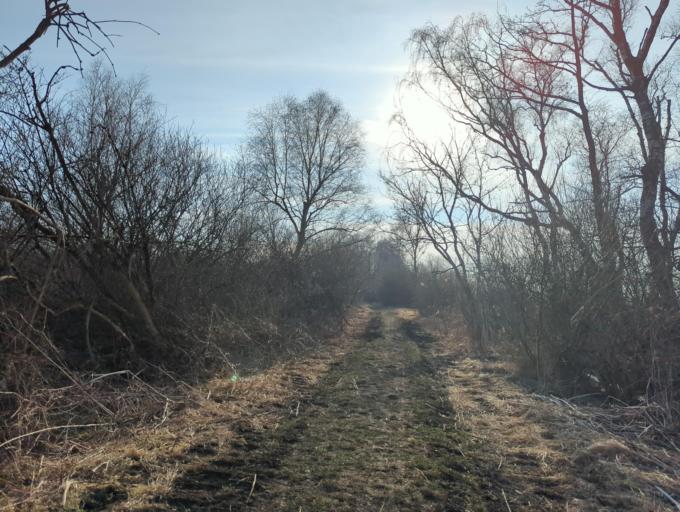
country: DE
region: Bavaria
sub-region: Swabia
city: Leipheim
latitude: 48.4775
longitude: 10.2051
